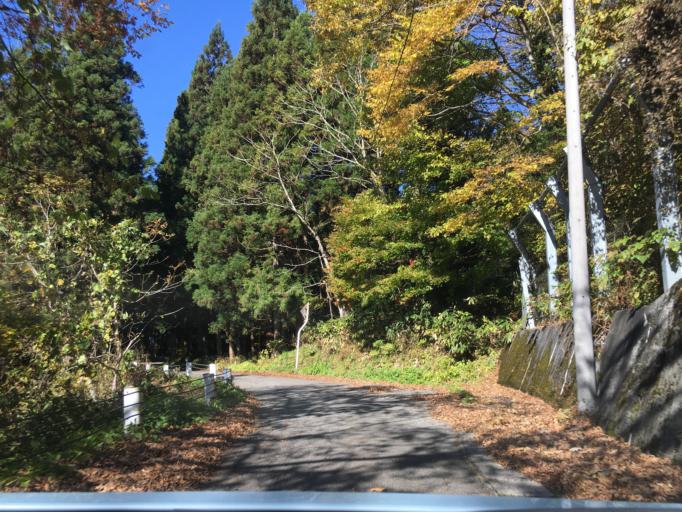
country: JP
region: Fukushima
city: Inawashiro
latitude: 37.4012
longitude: 140.0020
